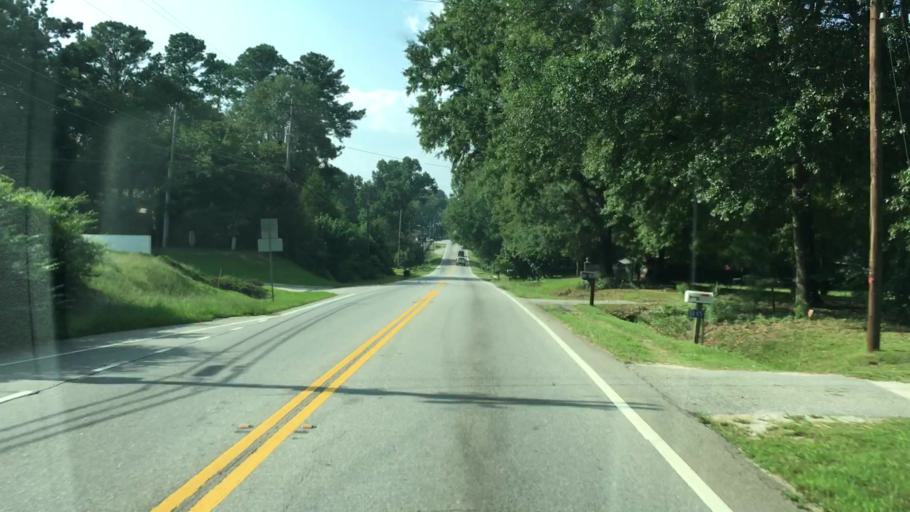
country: US
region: Georgia
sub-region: Walton County
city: Monroe
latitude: 33.7754
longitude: -83.7041
